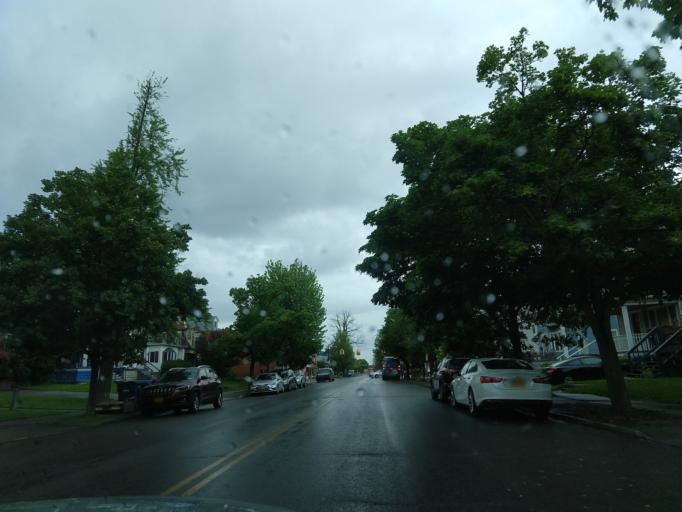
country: US
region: New York
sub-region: Erie County
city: Buffalo
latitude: 42.9251
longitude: -78.8771
